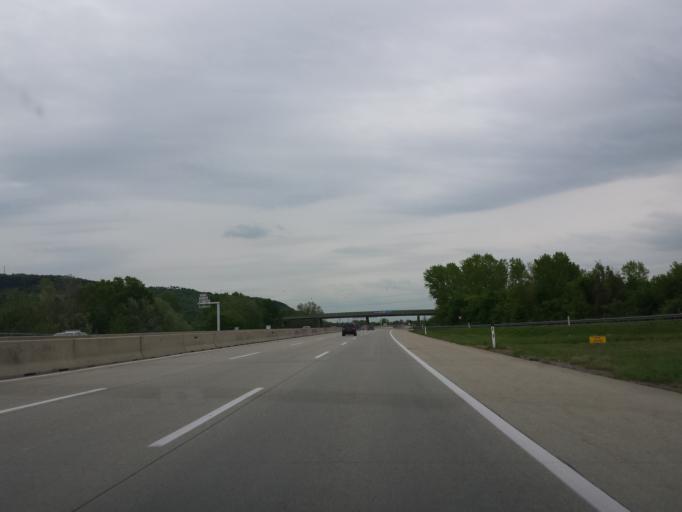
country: AT
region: Lower Austria
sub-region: Politischer Bezirk Korneuburg
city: Bisamberg
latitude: 48.3296
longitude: 16.3363
